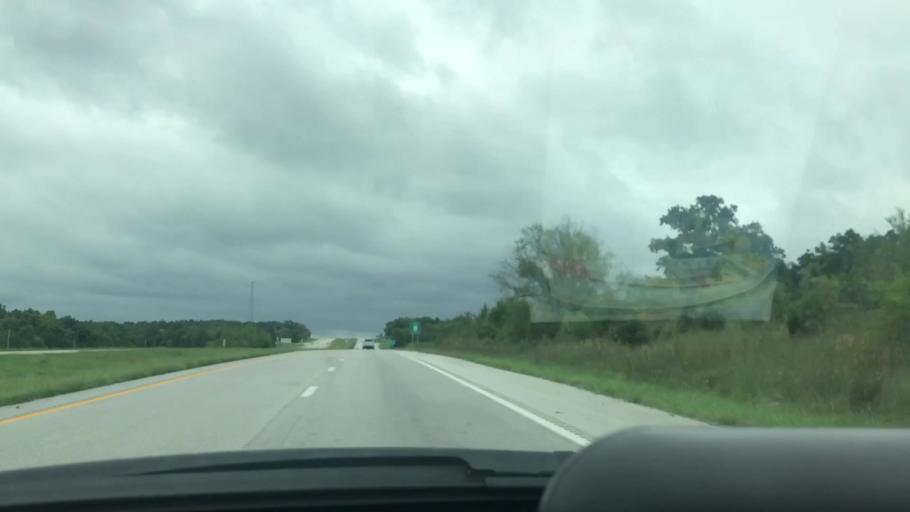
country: US
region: Missouri
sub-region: Greene County
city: Fair Grove
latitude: 37.4177
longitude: -93.1451
